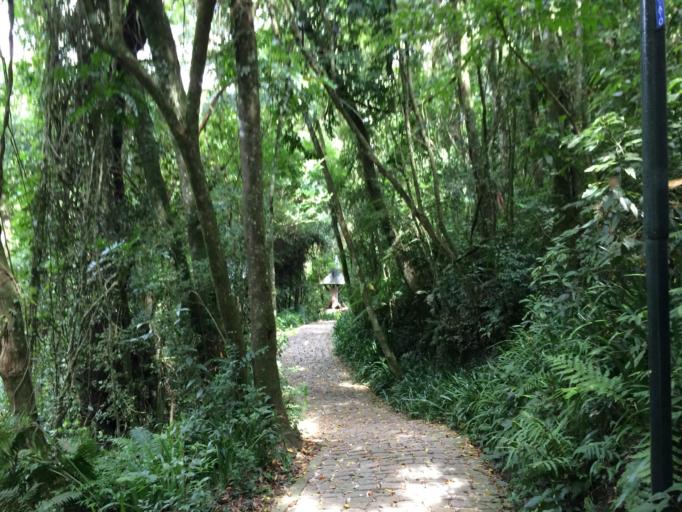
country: BR
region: Parana
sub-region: Curitiba
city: Curitiba
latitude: -25.4061
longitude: -49.2861
